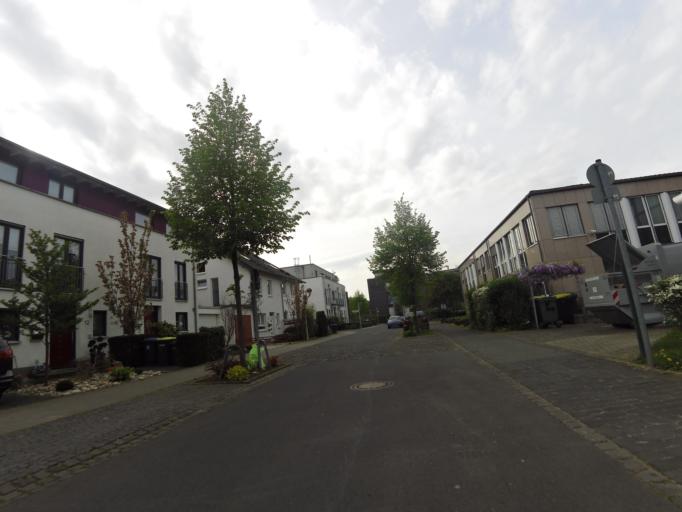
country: DE
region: North Rhine-Westphalia
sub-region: Regierungsbezirk Koln
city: Konigswinter
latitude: 50.7048
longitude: 7.1460
